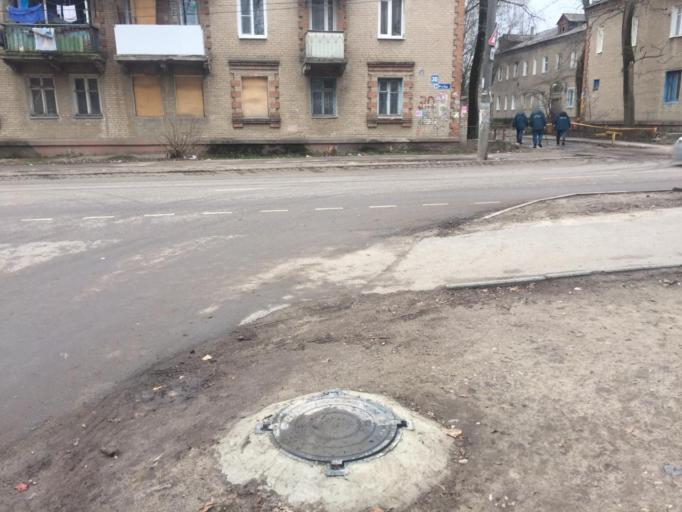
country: RU
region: Voronezj
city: Voronezh
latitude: 51.6771
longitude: 39.1532
